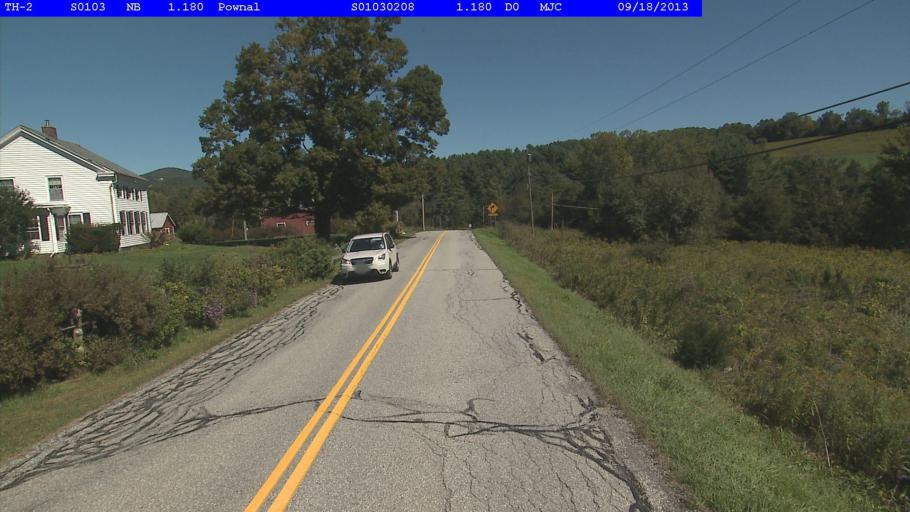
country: US
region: Vermont
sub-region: Bennington County
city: Bennington
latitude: 42.8035
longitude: -73.2482
